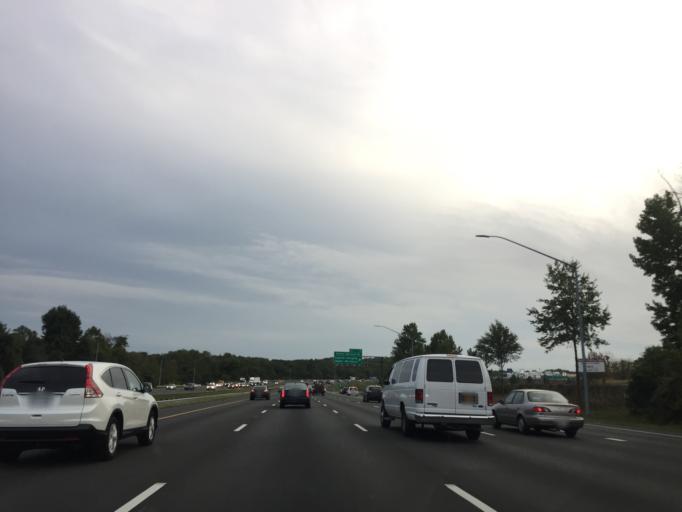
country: US
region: Maryland
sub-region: Prince George's County
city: Largo
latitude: 38.8746
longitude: -76.8439
